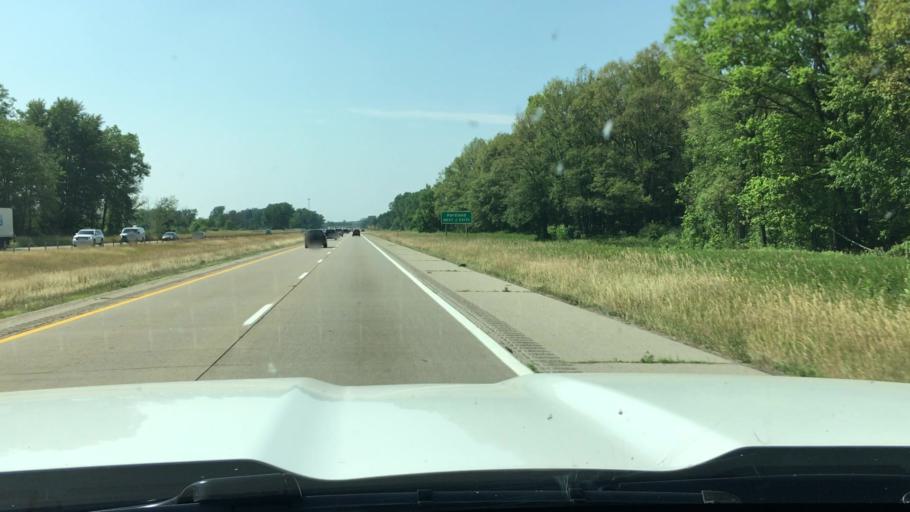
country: US
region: Michigan
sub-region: Ionia County
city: Portland
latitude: 42.8472
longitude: -84.8546
